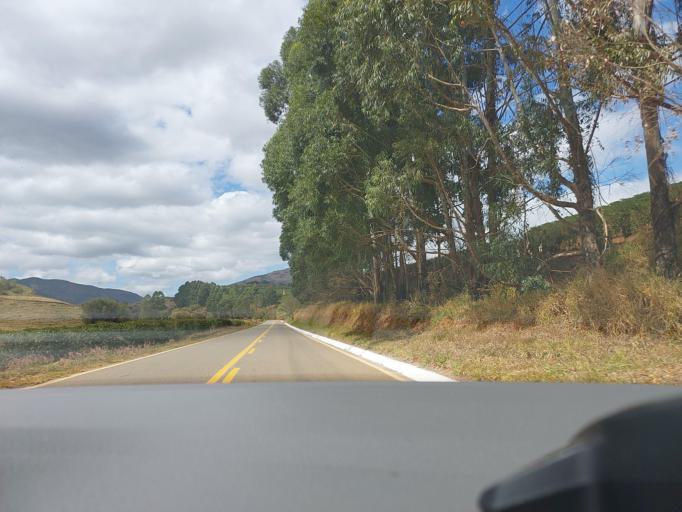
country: BR
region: Minas Gerais
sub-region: Visconde Do Rio Branco
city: Visconde do Rio Branco
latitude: -20.9436
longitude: -42.6264
